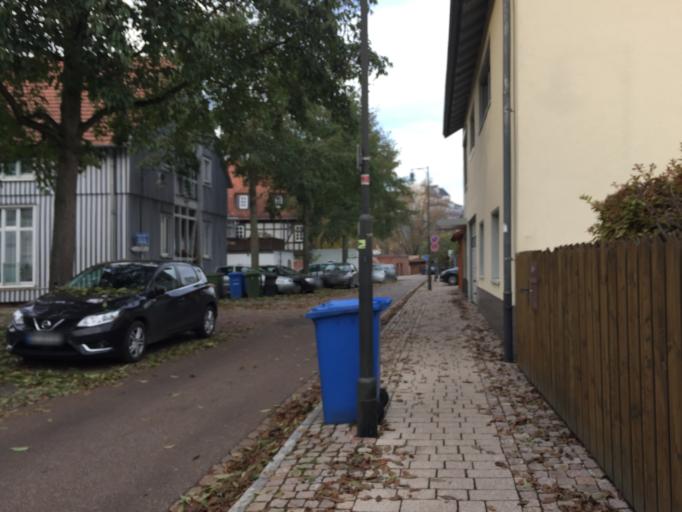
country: DE
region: Hesse
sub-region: Regierungsbezirk Giessen
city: Marburg an der Lahn
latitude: 50.8063
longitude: 8.7741
